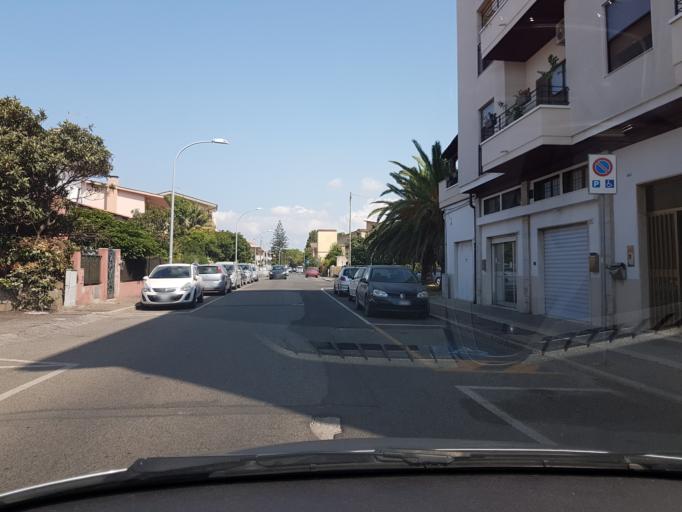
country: IT
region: Sardinia
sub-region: Provincia di Oristano
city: Oristano
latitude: 39.9099
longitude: 8.5908
